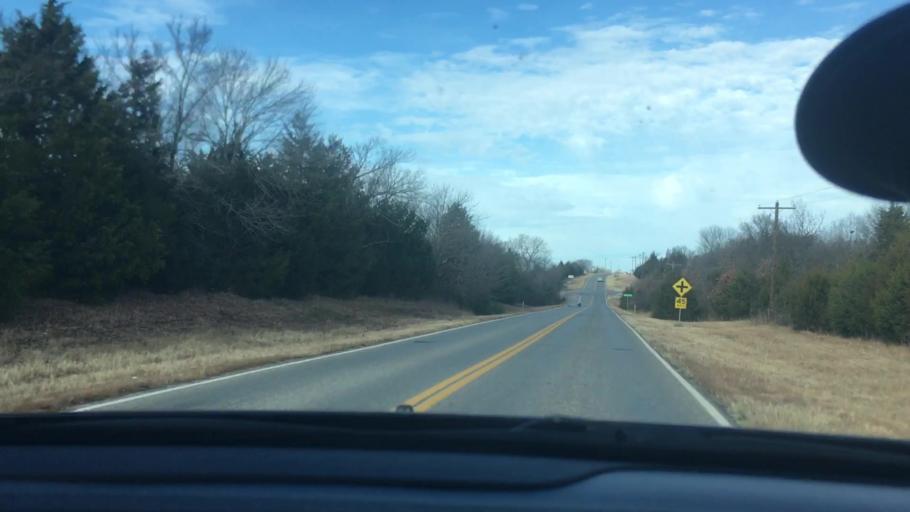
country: US
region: Oklahoma
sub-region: Seminole County
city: Konawa
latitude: 34.9678
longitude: -96.7730
